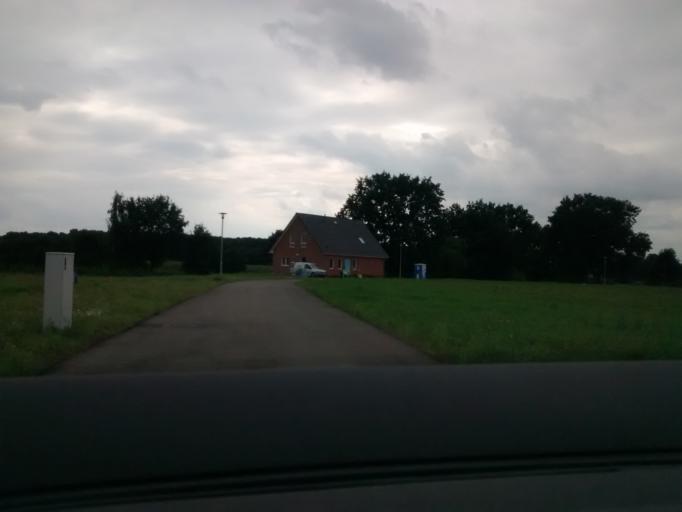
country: DE
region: Lower Saxony
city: Echem
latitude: 53.3382
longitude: 10.5497
